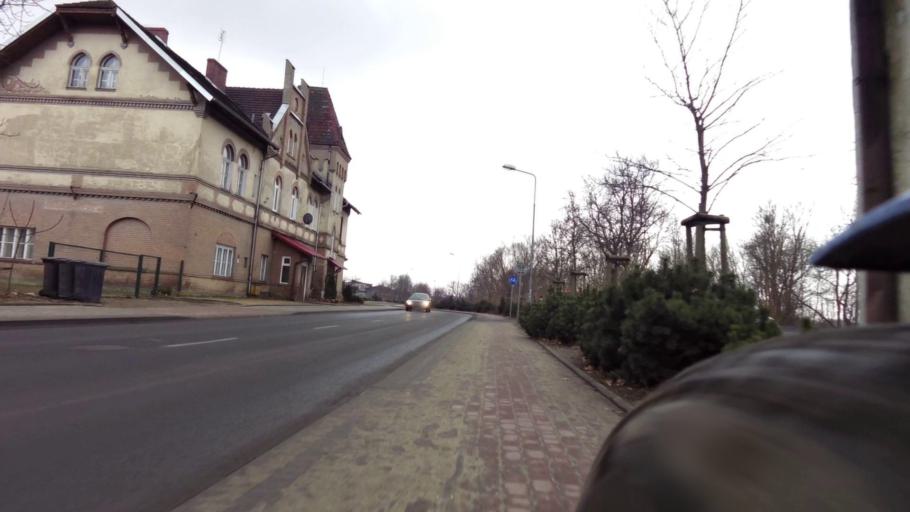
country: PL
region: West Pomeranian Voivodeship
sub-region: Powiat walecki
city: Walcz
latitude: 53.2703
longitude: 16.4850
